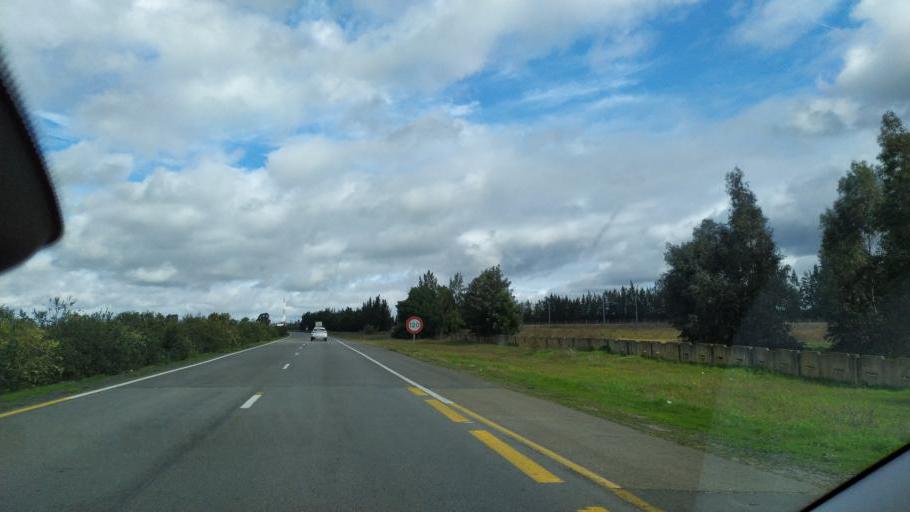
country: MA
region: Gharb-Chrarda-Beni Hssen
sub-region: Kenitra Province
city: Lalla Mimouna
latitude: 34.8810
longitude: -6.2117
